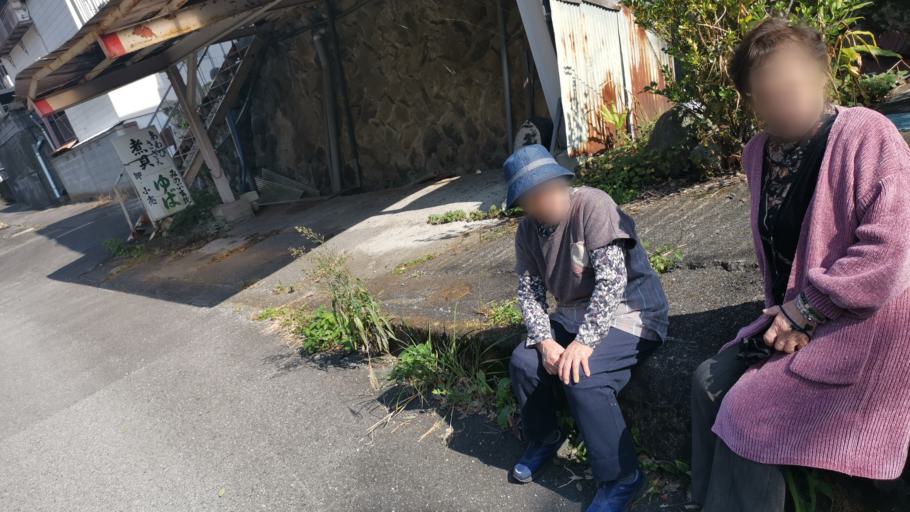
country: JP
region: Shizuoka
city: Fujinomiya
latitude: 35.3748
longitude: 138.4250
